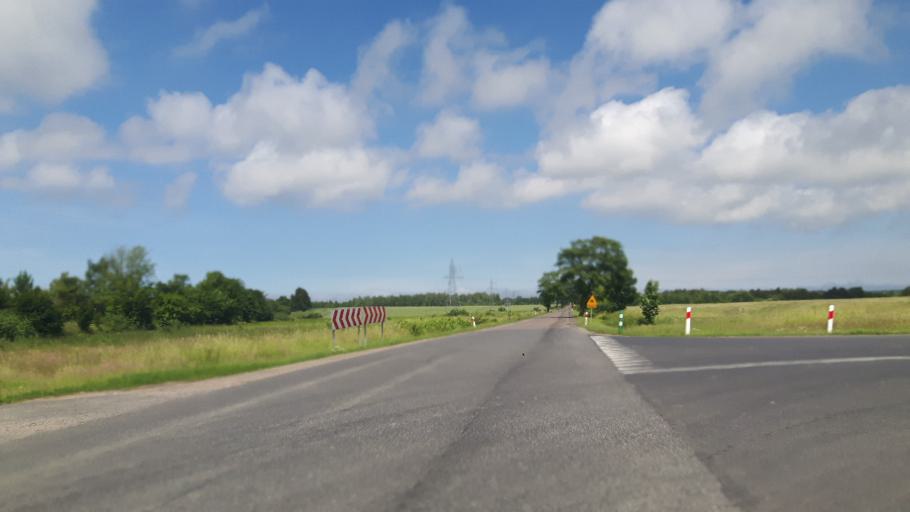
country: PL
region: Pomeranian Voivodeship
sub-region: Powiat slupski
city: Ustka
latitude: 54.5530
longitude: 16.8368
